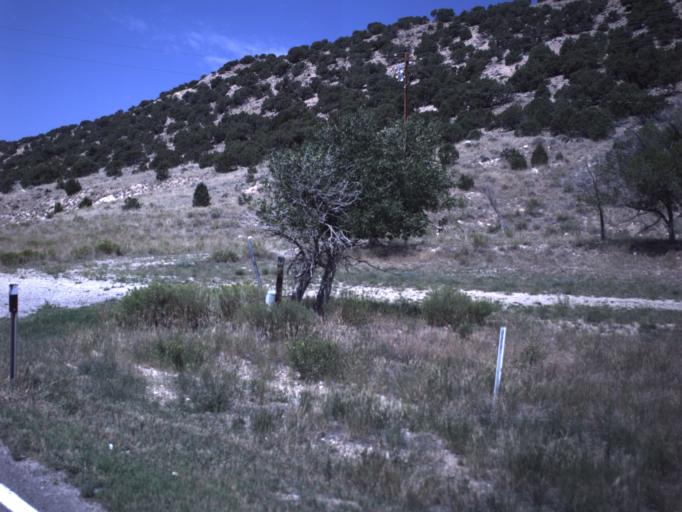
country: US
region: Utah
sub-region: Daggett County
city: Manila
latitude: 40.9824
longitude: -109.7421
